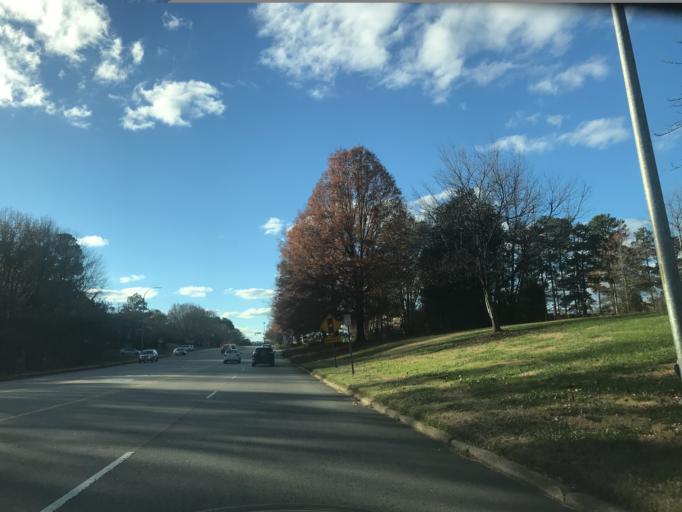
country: US
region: North Carolina
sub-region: Wake County
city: Raleigh
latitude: 35.8479
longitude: -78.5936
